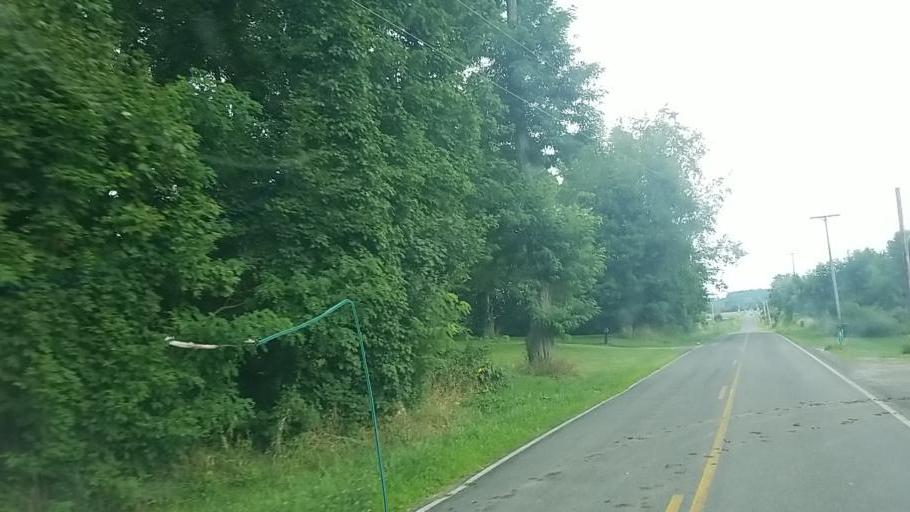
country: US
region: Ohio
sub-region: Medina County
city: Westfield Center
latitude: 41.0065
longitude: -81.9411
